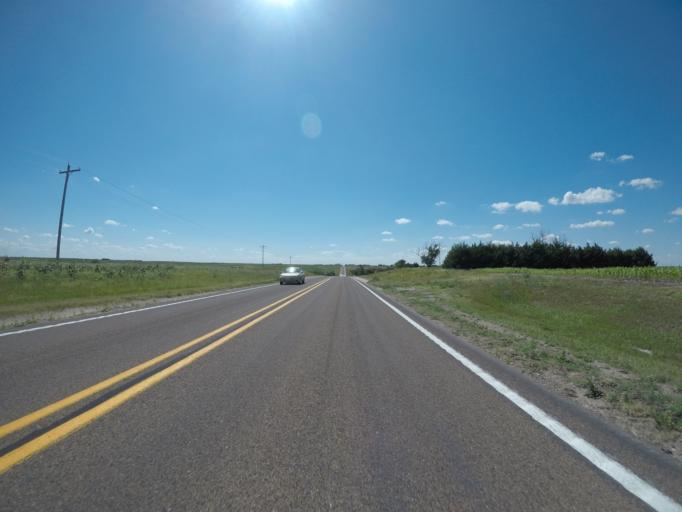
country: US
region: Nebraska
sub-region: Chase County
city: Imperial
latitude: 40.5376
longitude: -101.7575
